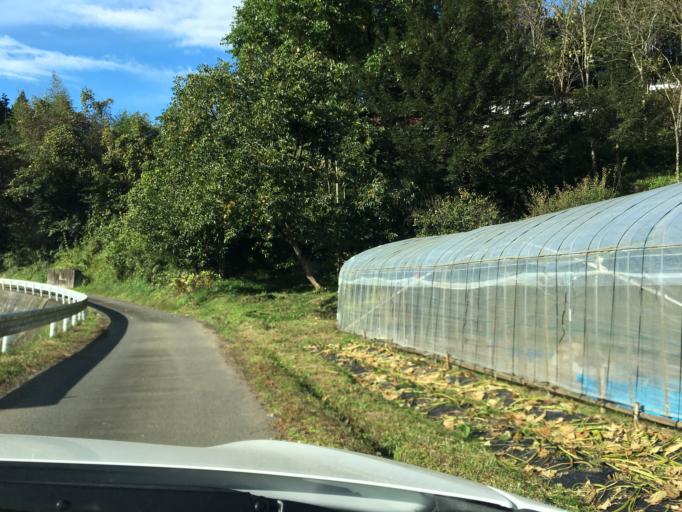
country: JP
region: Fukushima
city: Ishikawa
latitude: 37.1600
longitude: 140.5115
